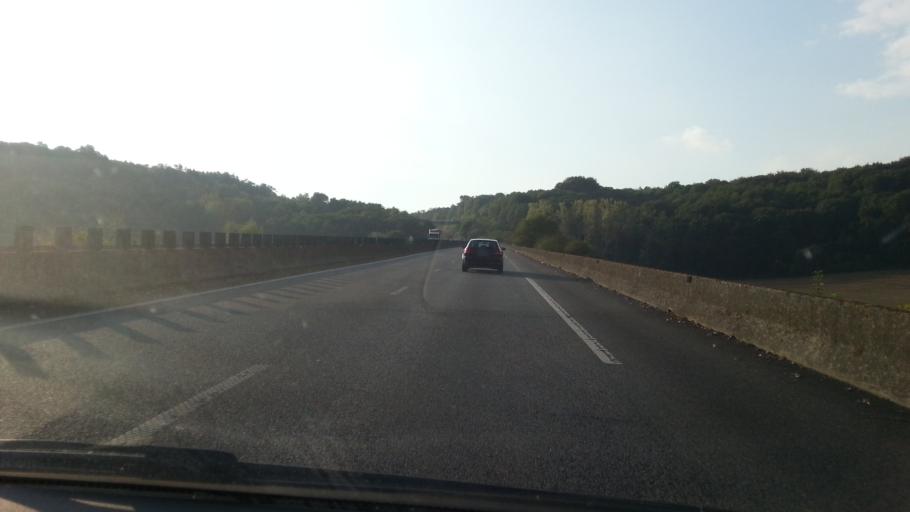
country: FR
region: Picardie
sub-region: Departement de l'Oise
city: Cambronne-les-Ribecourt
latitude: 49.5186
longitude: 2.9117
